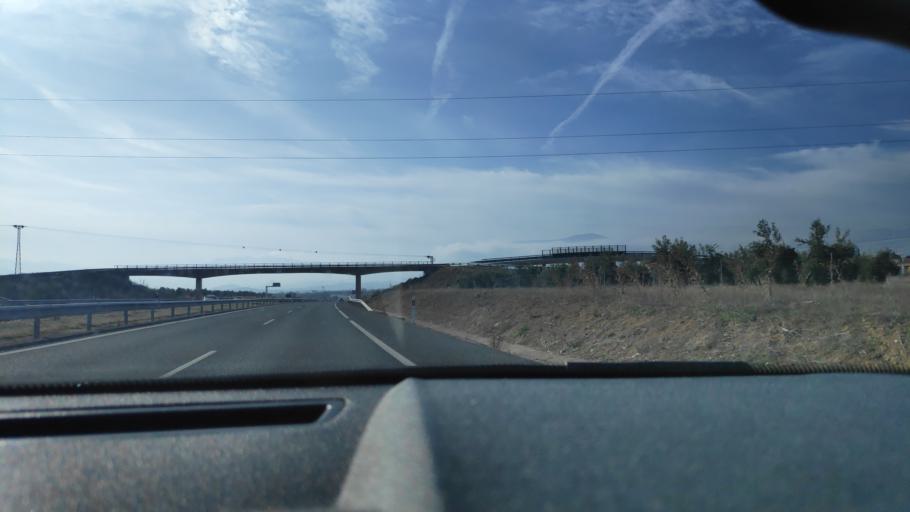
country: ES
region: Andalusia
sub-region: Provincia de Jaen
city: Jaen
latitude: 37.8389
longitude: -3.7639
